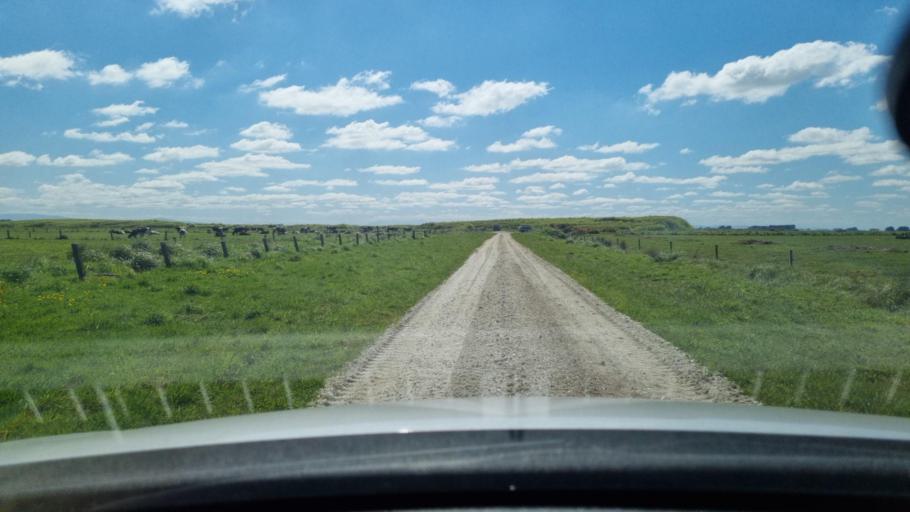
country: NZ
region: Southland
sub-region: Invercargill City
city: Invercargill
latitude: -46.3860
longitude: 168.2577
